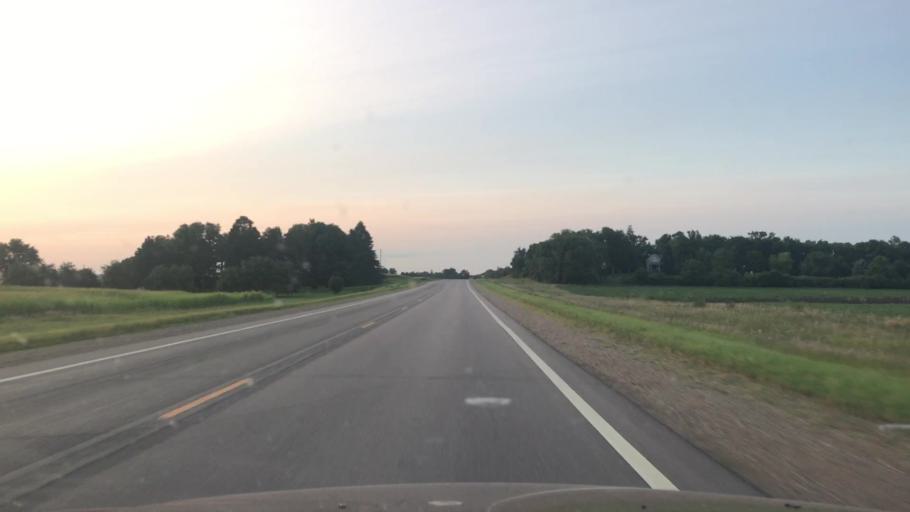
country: US
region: Minnesota
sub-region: Redwood County
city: Redwood Falls
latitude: 44.5156
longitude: -95.1181
